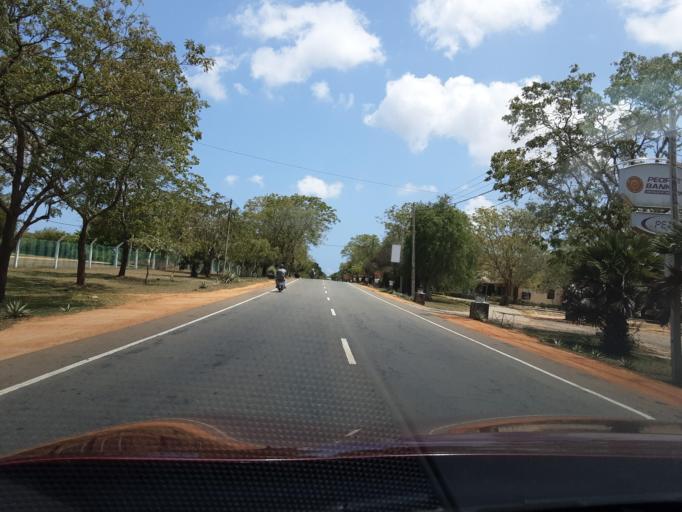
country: LK
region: Southern
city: Tangalla
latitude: 6.2524
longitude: 81.2275
